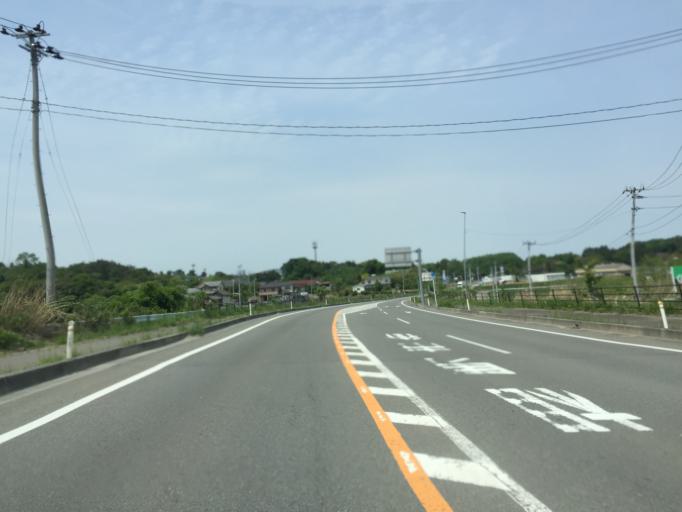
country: JP
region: Miyagi
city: Marumori
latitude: 37.8558
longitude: 140.9200
